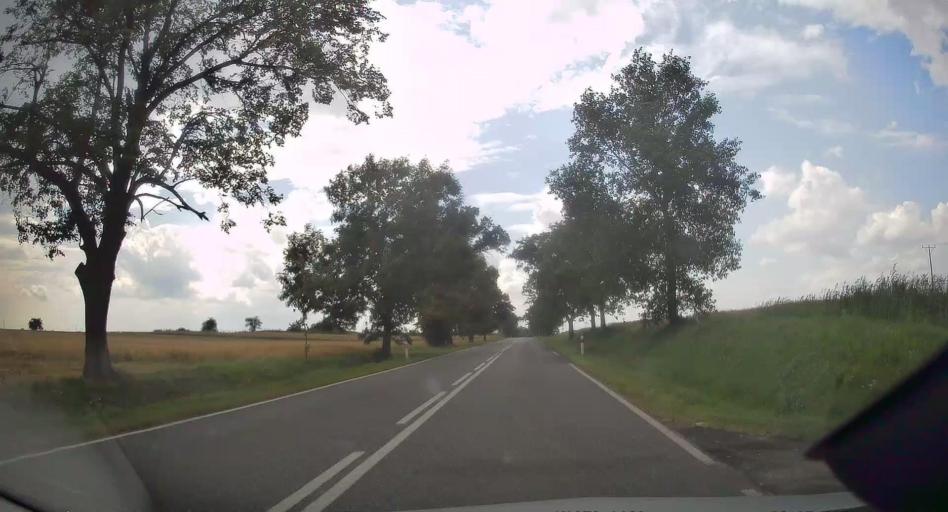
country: PL
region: Lodz Voivodeship
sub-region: Powiat skierniewicki
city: Gluchow
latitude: 51.7783
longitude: 20.0961
